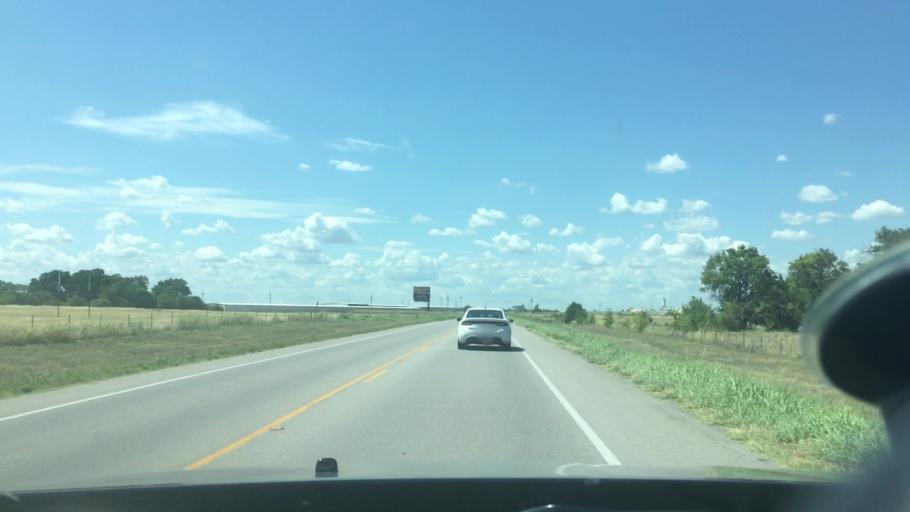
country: US
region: Oklahoma
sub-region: Marshall County
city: Kingston
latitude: 34.0466
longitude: -96.7401
